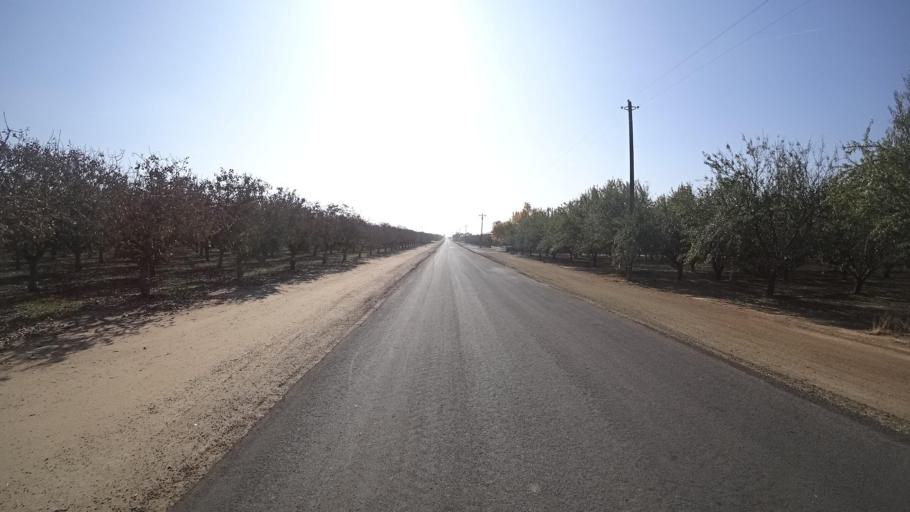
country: US
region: California
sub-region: Kern County
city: McFarland
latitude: 35.6429
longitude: -119.1867
